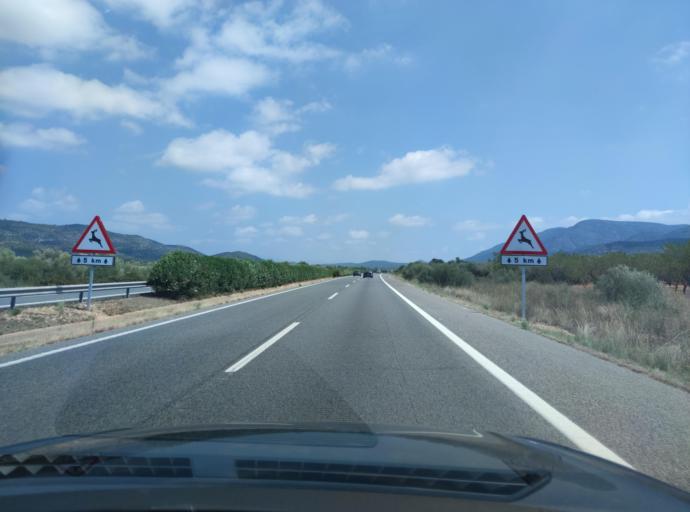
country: ES
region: Catalonia
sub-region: Provincia de Tarragona
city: Ulldecona
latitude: 40.6163
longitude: 0.4813
